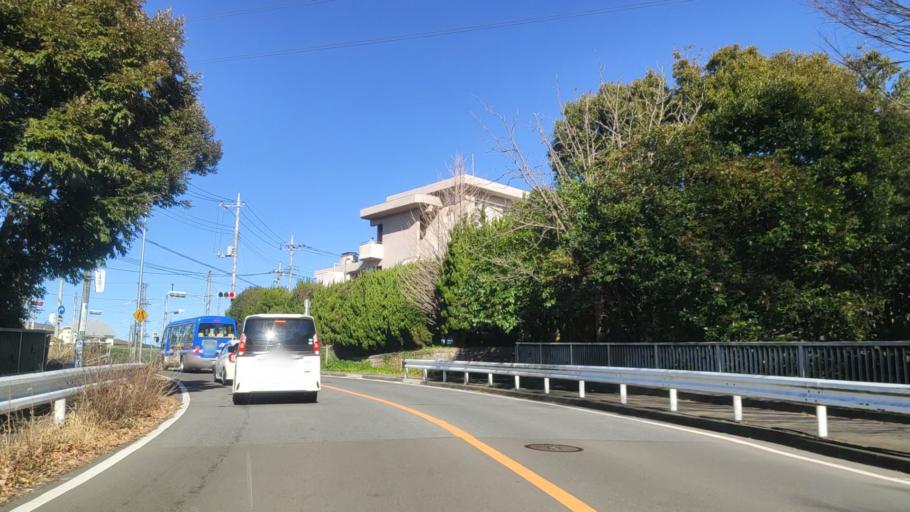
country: JP
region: Kanagawa
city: Minami-rinkan
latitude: 35.5083
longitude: 139.4989
